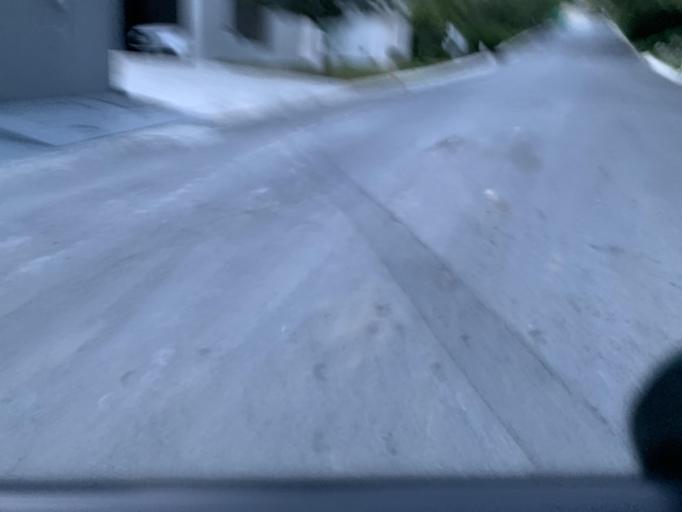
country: MX
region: Nuevo Leon
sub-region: Juarez
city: Bosques de San Pedro
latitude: 25.5196
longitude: -100.1884
